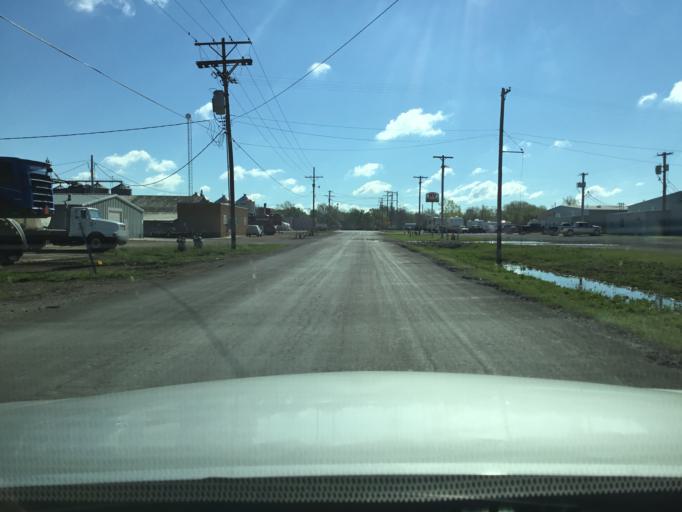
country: US
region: Kansas
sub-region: Allen County
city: Iola
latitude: 37.9285
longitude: -95.4132
